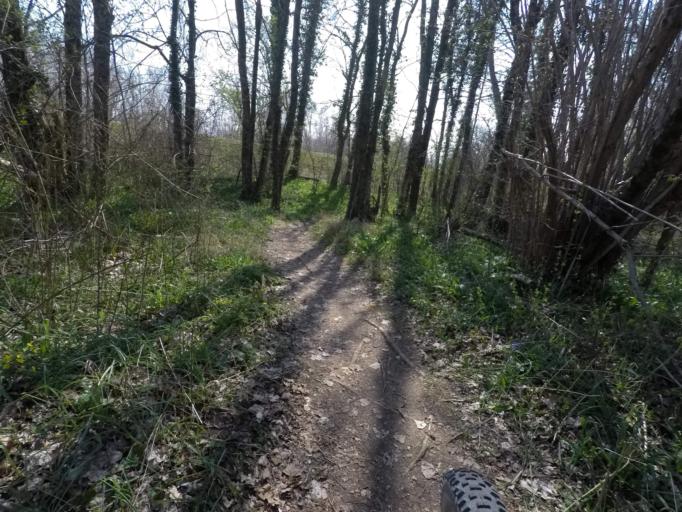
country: IT
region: Friuli Venezia Giulia
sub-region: Provincia di Udine
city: Remanzacco
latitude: 46.0627
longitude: 13.3287
